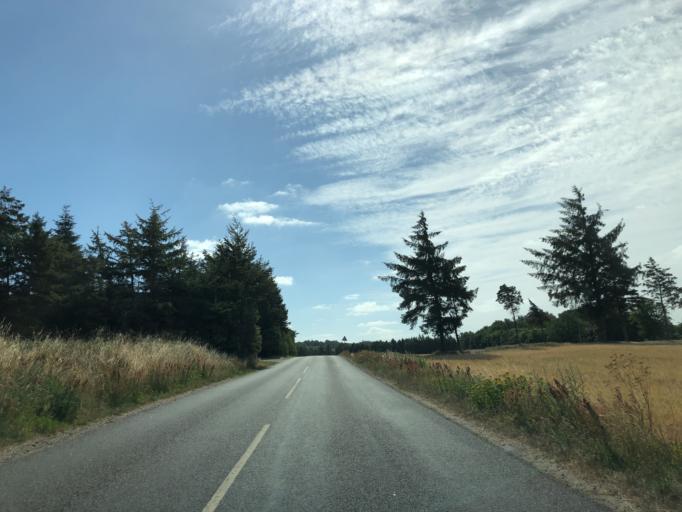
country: DK
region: North Denmark
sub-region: Vesthimmerland Kommune
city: Alestrup
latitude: 56.5772
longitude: 9.5131
